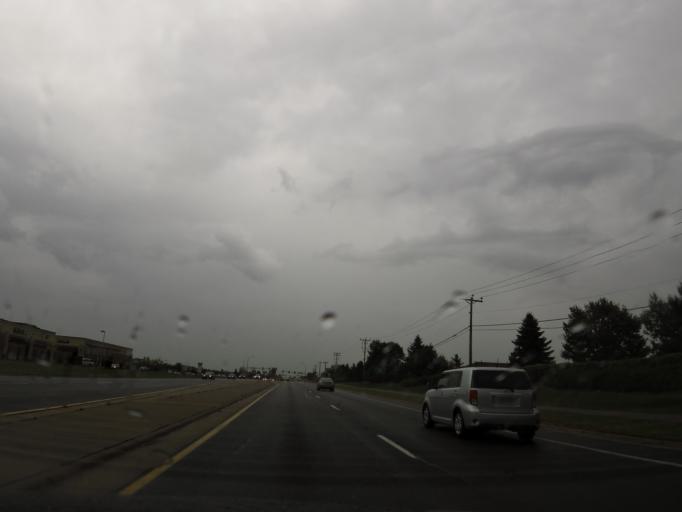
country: US
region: Minnesota
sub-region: Washington County
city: Woodbury
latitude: 44.9390
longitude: -92.9034
